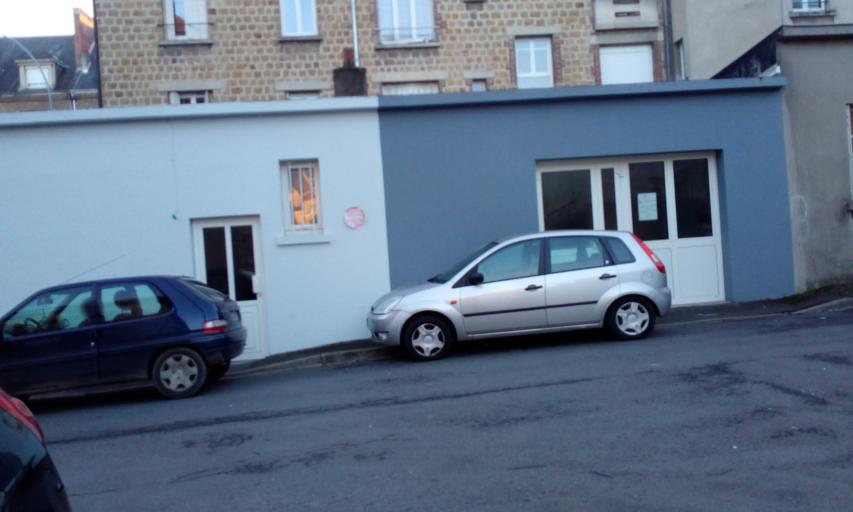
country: FR
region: Champagne-Ardenne
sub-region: Departement des Ardennes
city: Charleville-Mezieres
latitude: 49.7742
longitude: 4.7194
